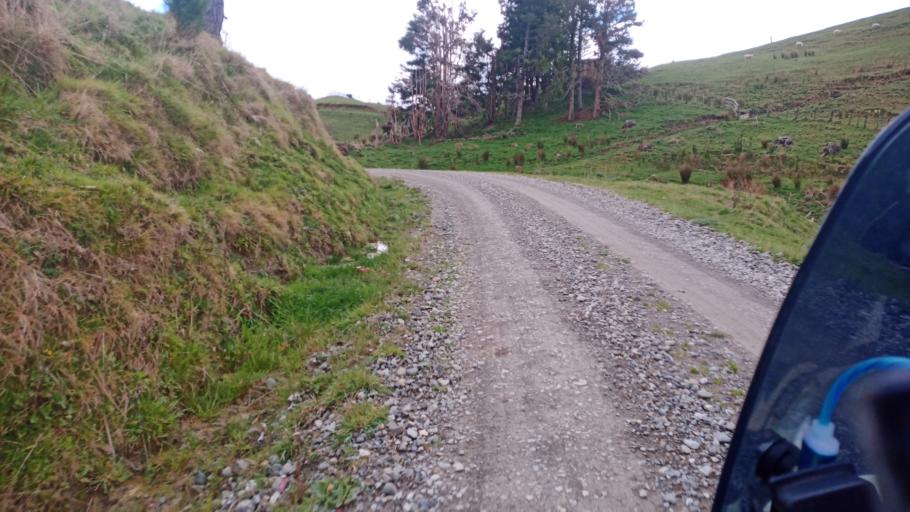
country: NZ
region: Gisborne
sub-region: Gisborne District
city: Gisborne
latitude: -38.5463
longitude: 178.1384
